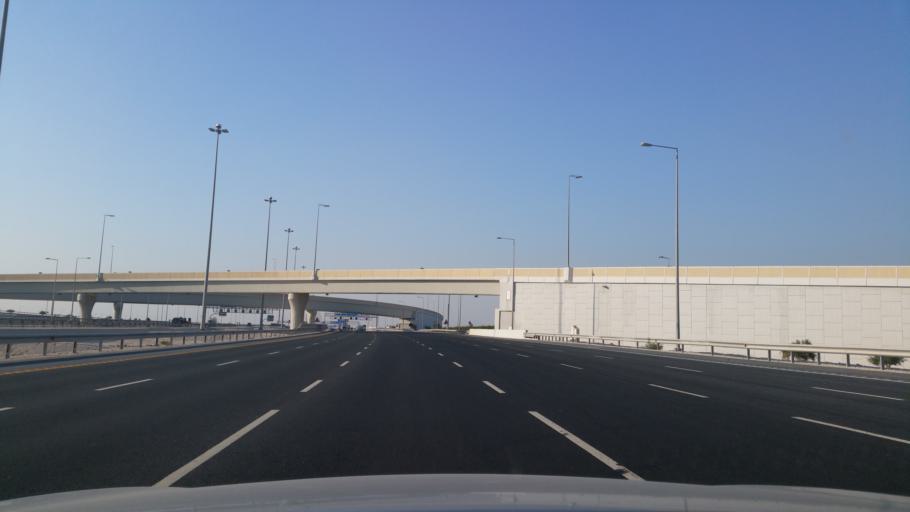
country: QA
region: Al Wakrah
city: Al Wakrah
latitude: 25.1326
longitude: 51.5860
